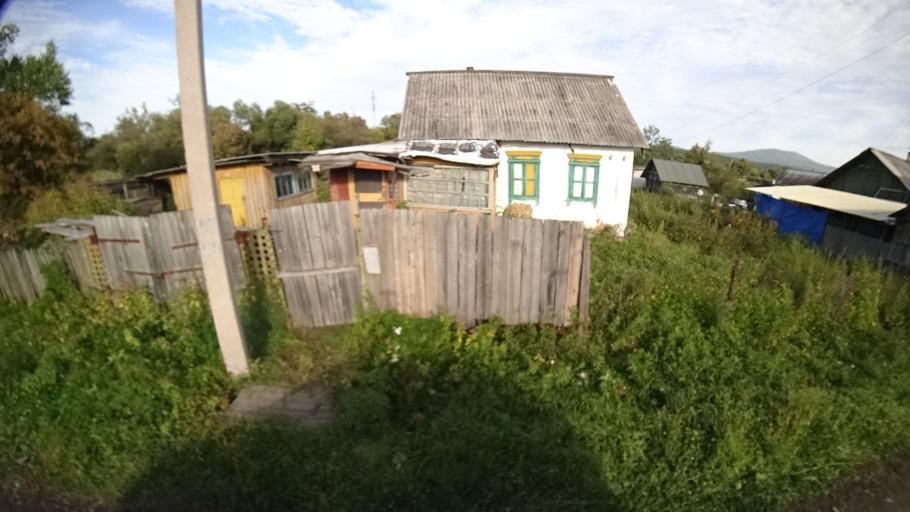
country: RU
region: Primorskiy
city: Dostoyevka
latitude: 44.2918
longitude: 133.4301
